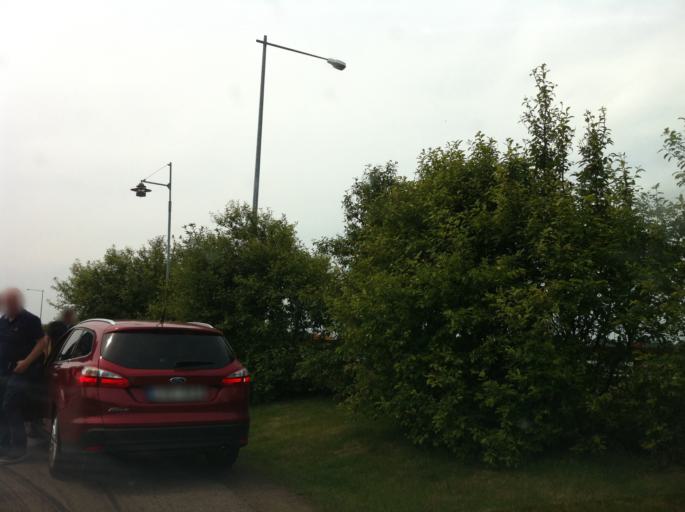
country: SE
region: Kalmar
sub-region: Torsas Kommun
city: Torsas
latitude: 56.3223
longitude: 16.0335
